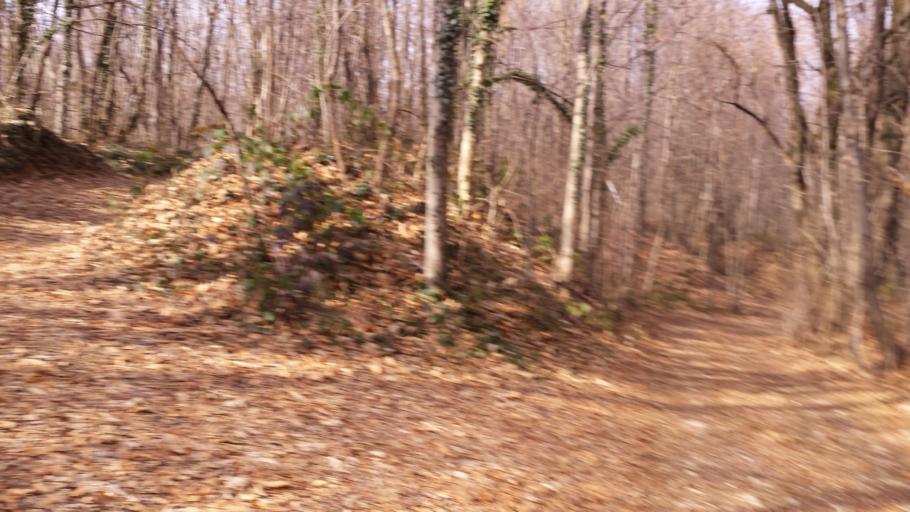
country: IT
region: Veneto
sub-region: Provincia di Treviso
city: Paderno del Grappa
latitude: 45.8482
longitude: 11.8541
